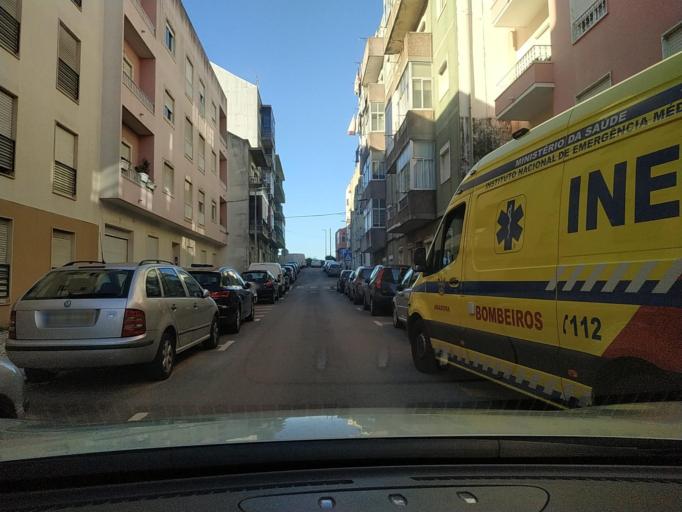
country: PT
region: Lisbon
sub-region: Odivelas
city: Famoes
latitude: 38.7709
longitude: -9.2200
